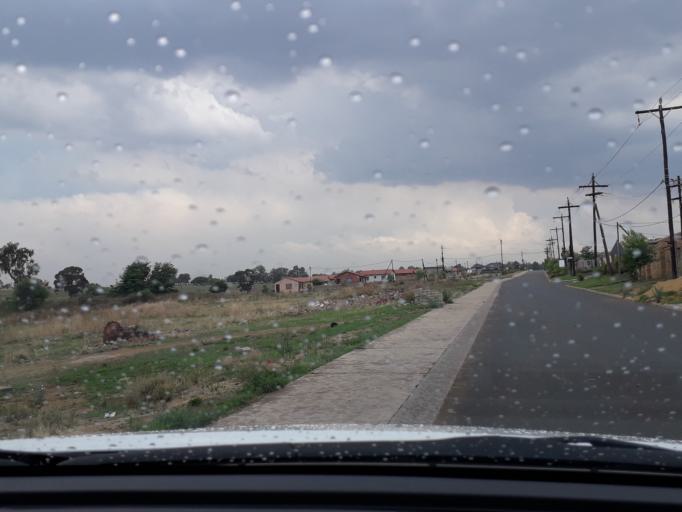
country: ZA
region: Gauteng
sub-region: West Rand District Municipality
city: Muldersdriseloop
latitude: -26.0048
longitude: 27.8530
